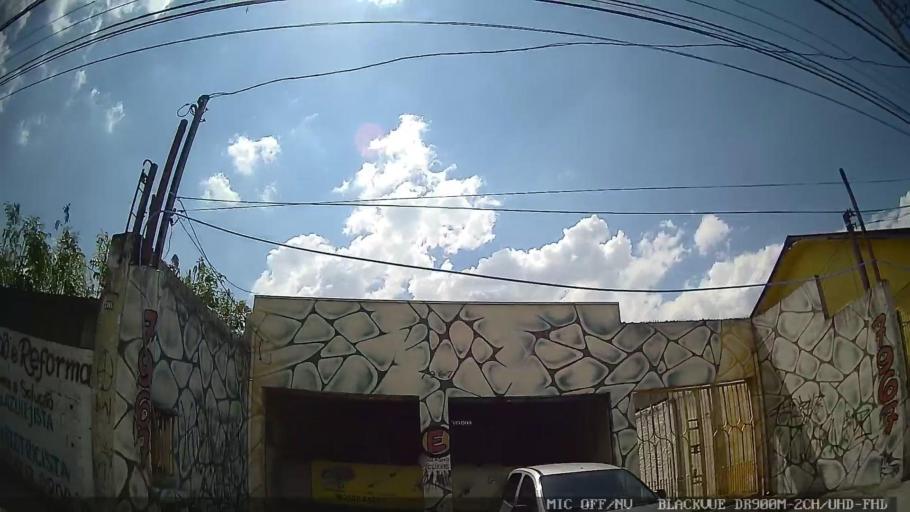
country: BR
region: Sao Paulo
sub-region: Ferraz De Vasconcelos
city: Ferraz de Vasconcelos
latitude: -23.5418
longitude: -46.4579
